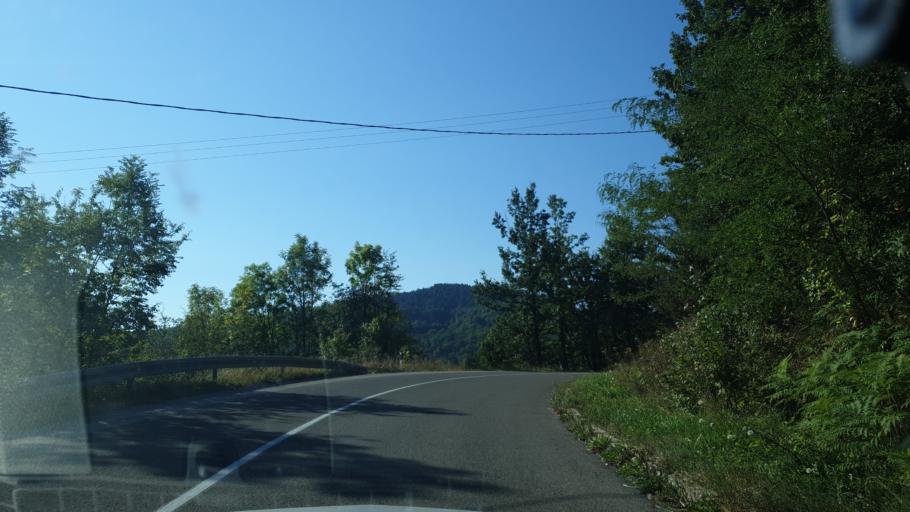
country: RS
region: Central Serbia
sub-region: Zlatiborski Okrug
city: Cajetina
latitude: 43.7218
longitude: 19.7983
